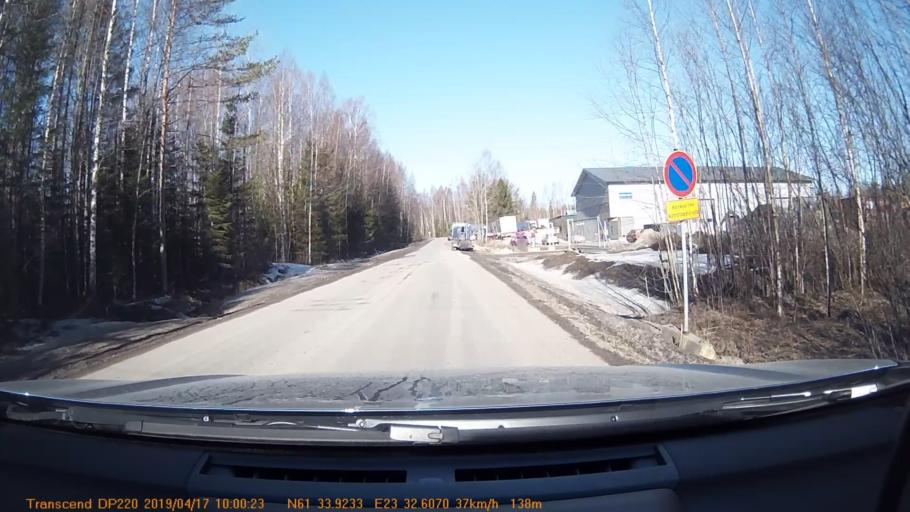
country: FI
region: Pirkanmaa
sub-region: Tampere
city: Yloejaervi
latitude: 61.5654
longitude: 23.5435
